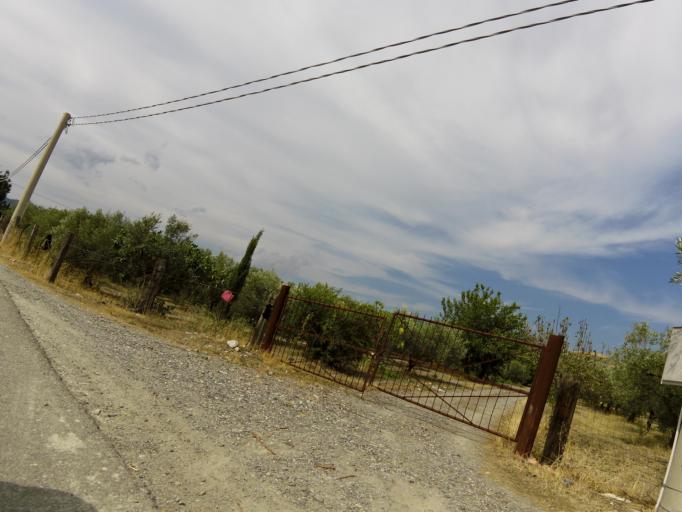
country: IT
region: Calabria
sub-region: Provincia di Reggio Calabria
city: Monasterace
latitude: 38.4532
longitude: 16.5178
